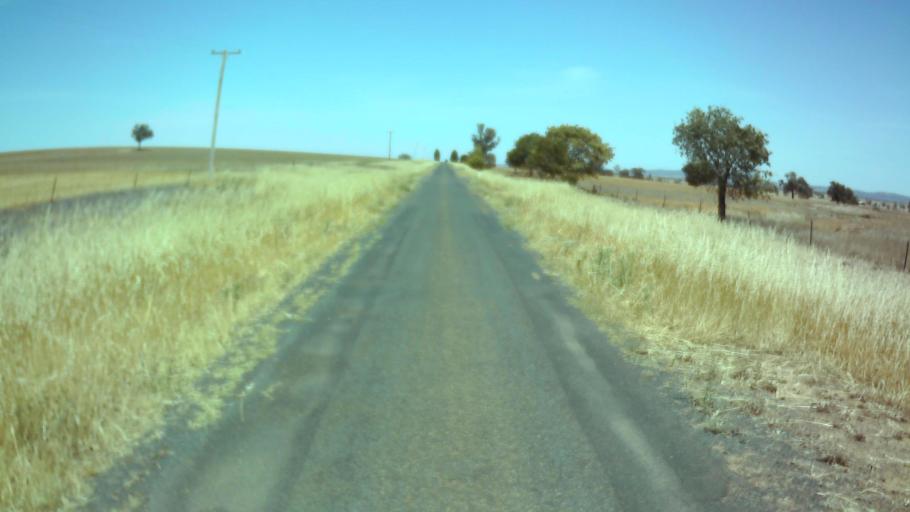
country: AU
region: New South Wales
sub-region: Weddin
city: Grenfell
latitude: -33.8635
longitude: 147.9914
